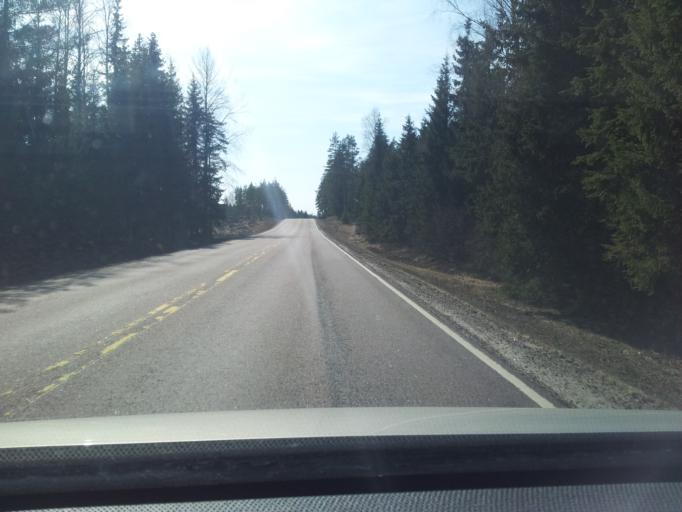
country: FI
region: Kymenlaakso
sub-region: Kotka-Hamina
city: Hamina
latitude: 60.7240
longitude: 27.3192
